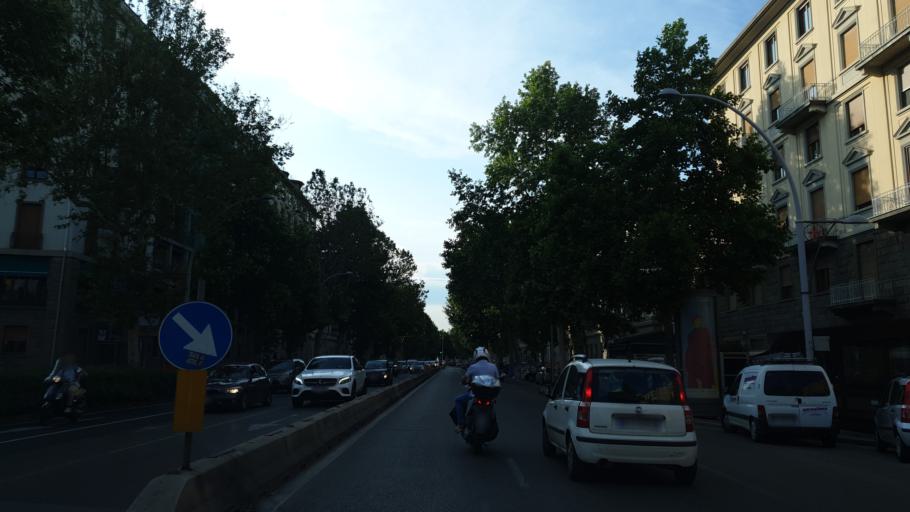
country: IT
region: Tuscany
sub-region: Province of Florence
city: Florence
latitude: 43.7803
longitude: 11.2653
